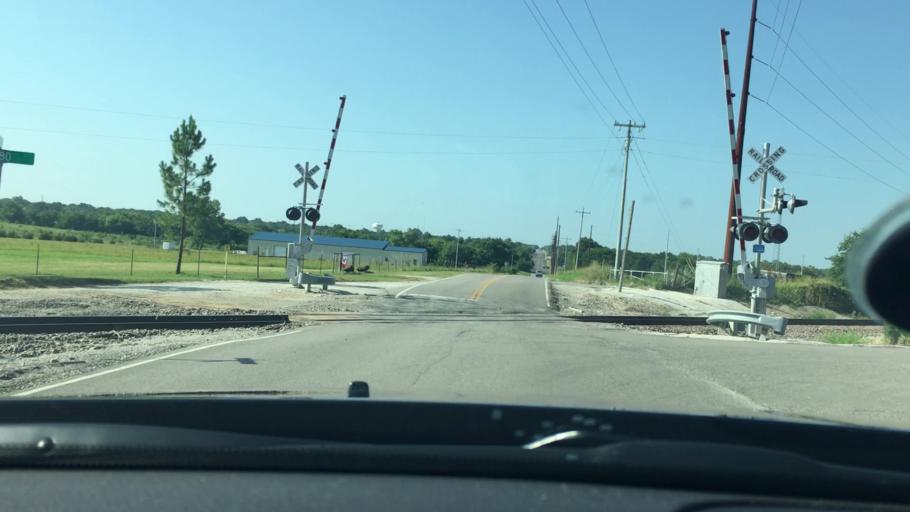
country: US
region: Oklahoma
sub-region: Pontotoc County
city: Ada
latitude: 34.7962
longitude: -96.6348
